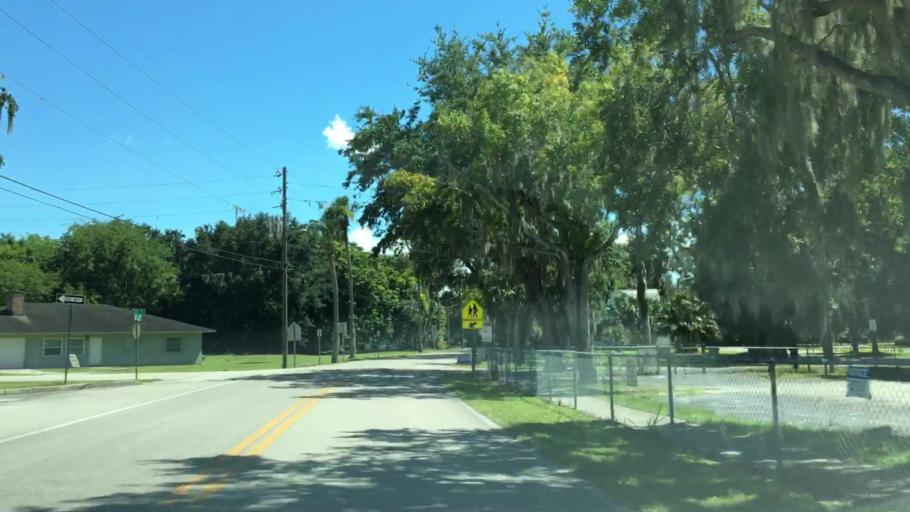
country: US
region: Florida
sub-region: Volusia County
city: Deltona
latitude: 28.8711
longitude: -81.2663
